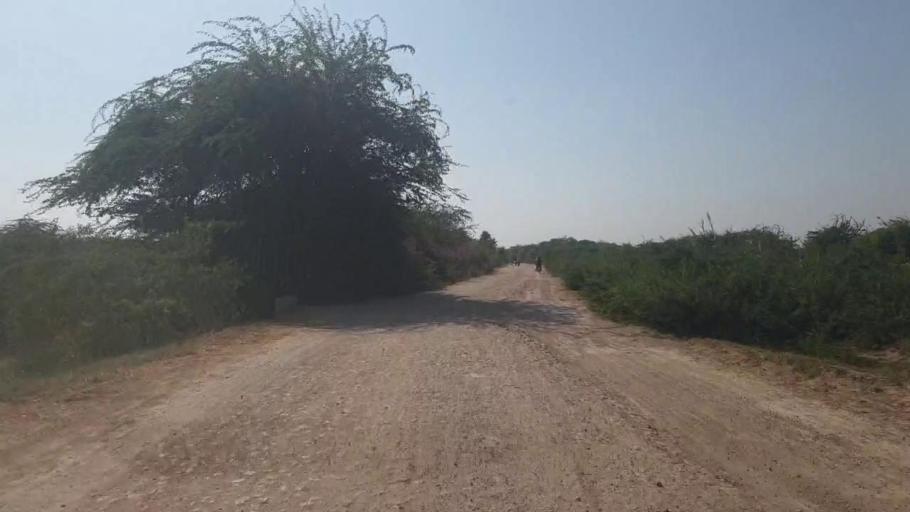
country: PK
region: Sindh
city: Badin
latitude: 24.5932
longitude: 68.8484
